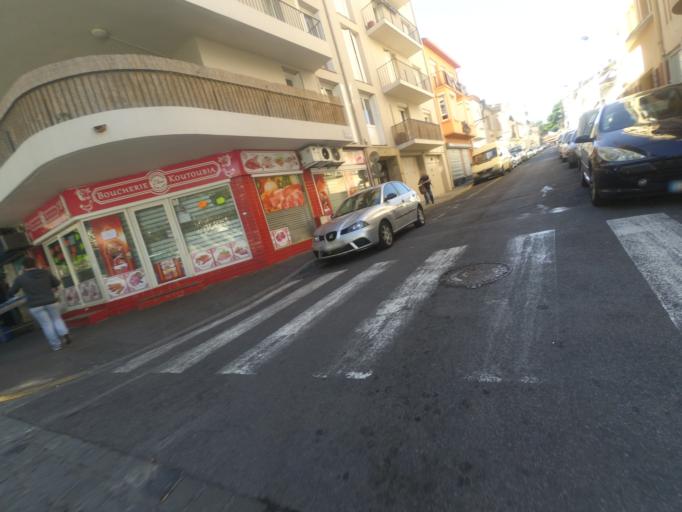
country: FR
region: Languedoc-Roussillon
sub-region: Departement des Pyrenees-Orientales
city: Perpignan
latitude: 42.6968
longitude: 2.9029
